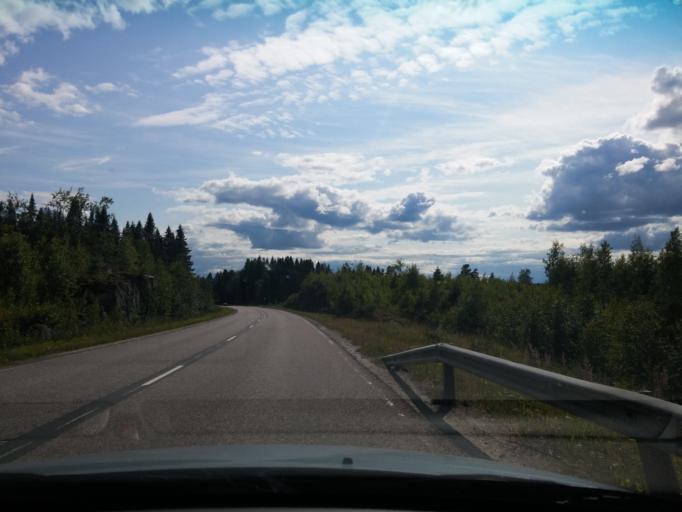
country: FI
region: Central Finland
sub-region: Keuruu
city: Keuruu
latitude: 62.2809
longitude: 24.6917
